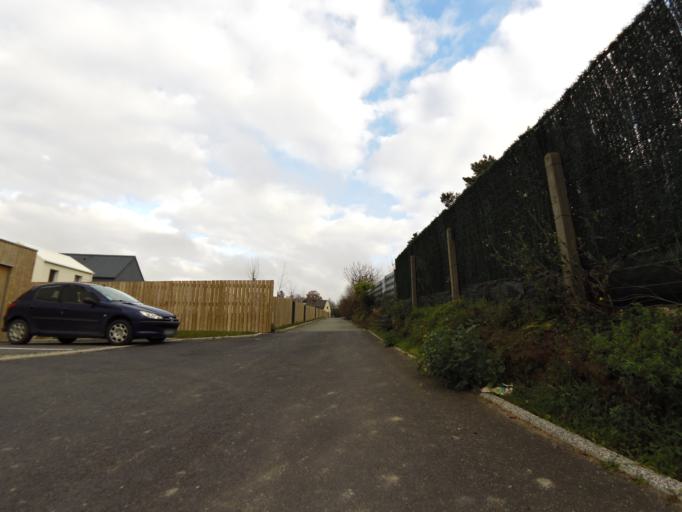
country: FR
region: Brittany
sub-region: Departement d'Ille-et-Vilaine
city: Orgeres
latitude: 47.9952
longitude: -1.6716
